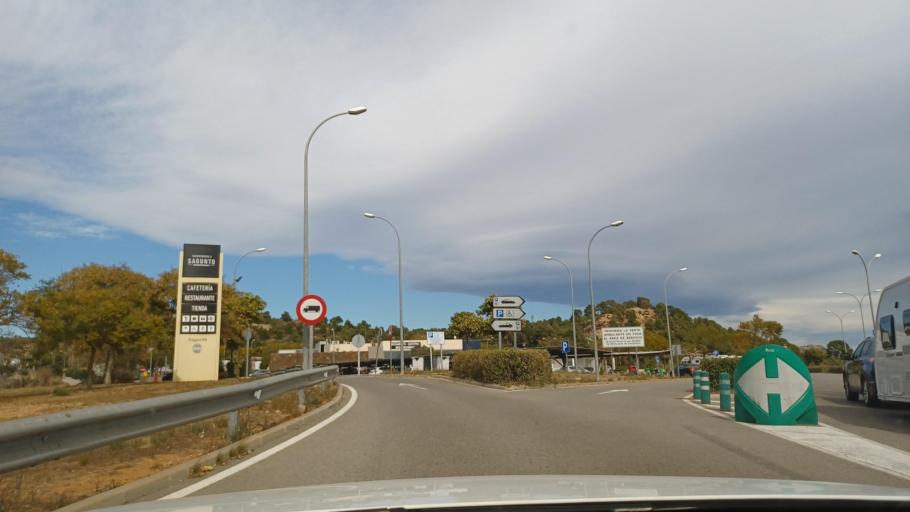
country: ES
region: Valencia
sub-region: Provincia de Valencia
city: Pucol
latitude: 39.6486
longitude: -0.3004
